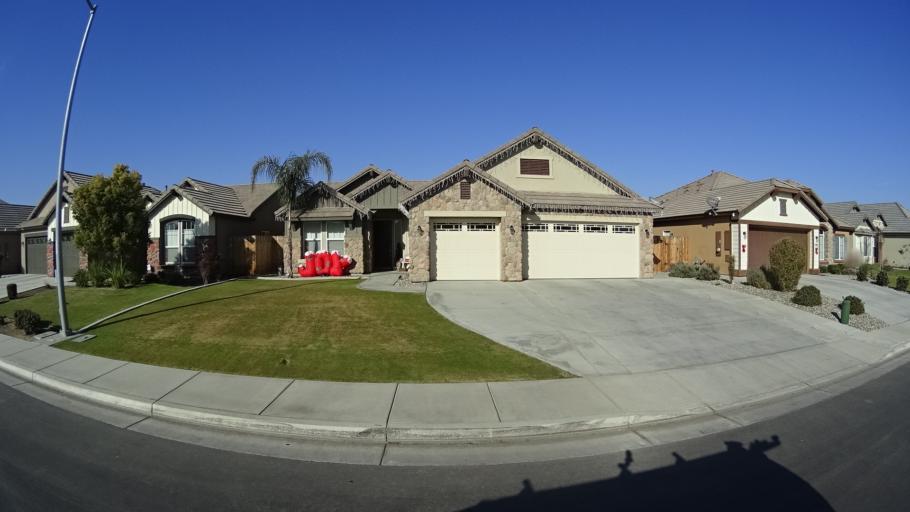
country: US
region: California
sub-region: Kern County
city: Greenacres
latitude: 35.3794
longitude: -119.1035
